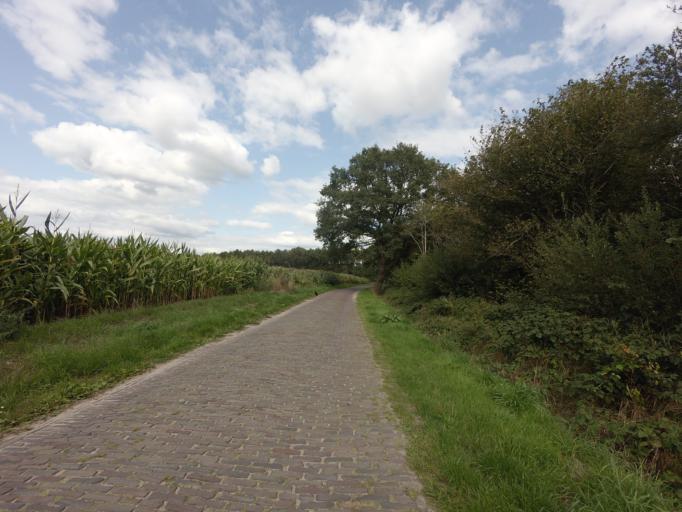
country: NL
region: Drenthe
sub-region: Gemeente De Wolden
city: Ruinen
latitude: 52.7675
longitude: 6.3643
